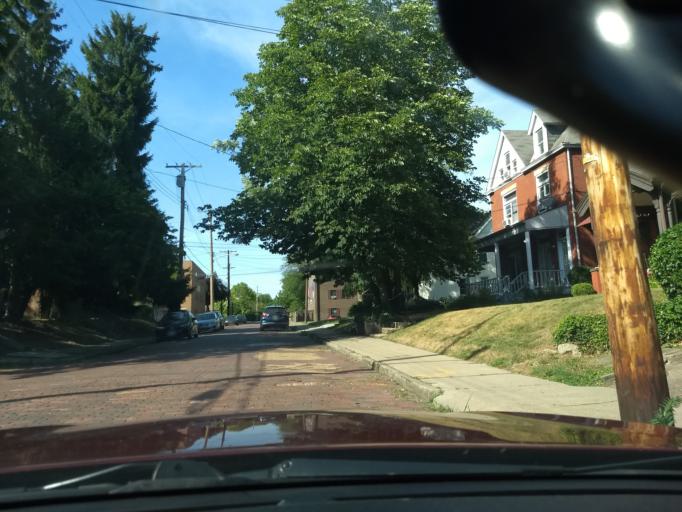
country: US
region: Pennsylvania
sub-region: Allegheny County
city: Wilkinsburg
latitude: 40.4392
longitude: -79.8886
